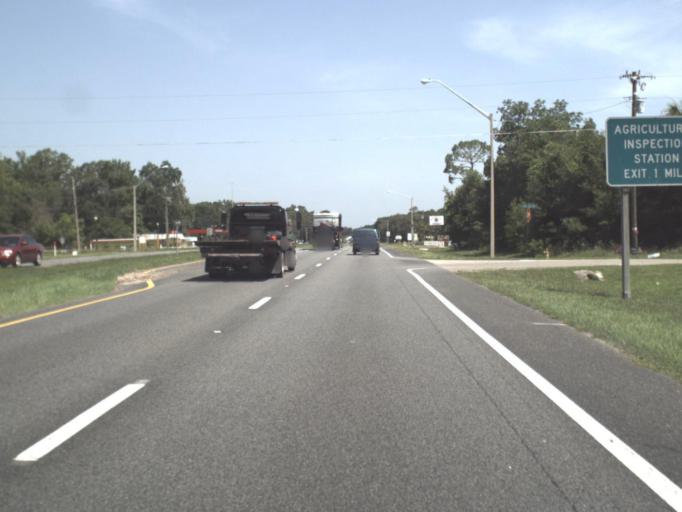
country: US
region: Florida
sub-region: Levy County
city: Manatee Road
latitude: 29.5799
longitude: -82.9180
